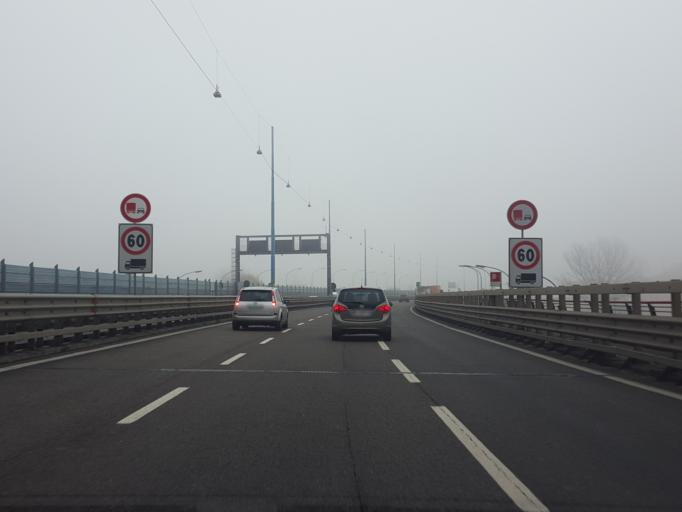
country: IT
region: Veneto
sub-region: Provincia di Venezia
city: Mestre
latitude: 45.4892
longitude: 12.2206
